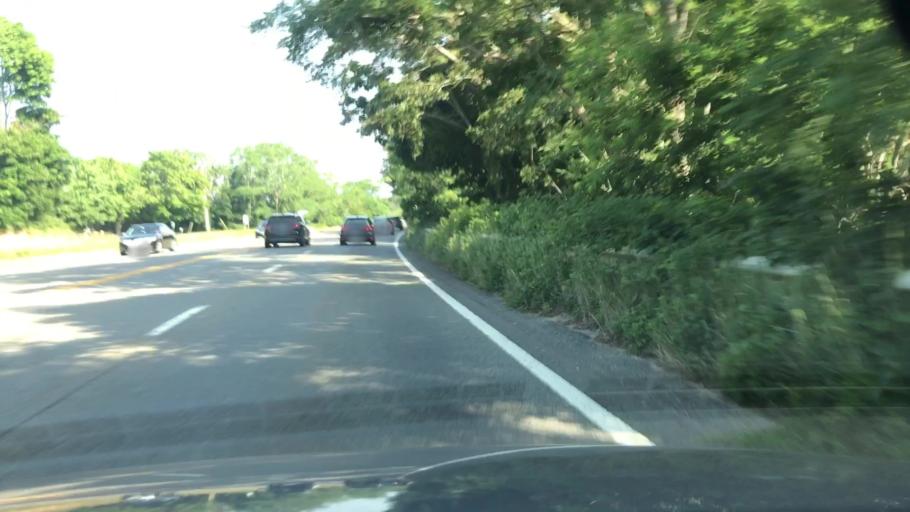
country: US
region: Massachusetts
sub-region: Barnstable County
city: Eastham
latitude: 41.8408
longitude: -69.9803
